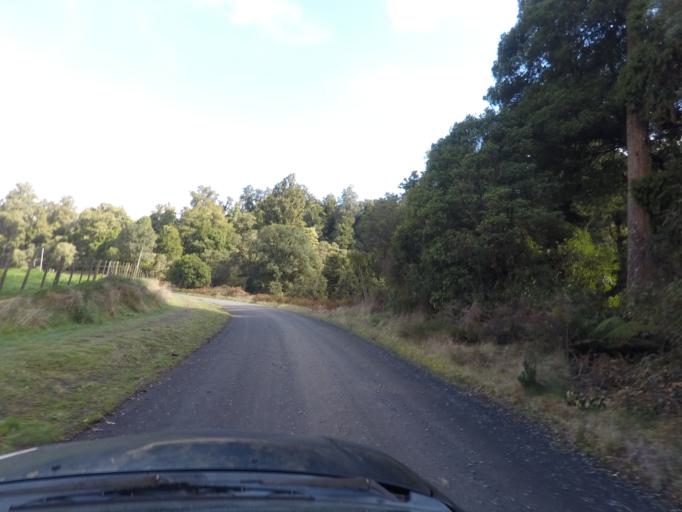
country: NZ
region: Manawatu-Wanganui
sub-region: Ruapehu District
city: Waiouru
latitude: -39.3945
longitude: 175.3962
